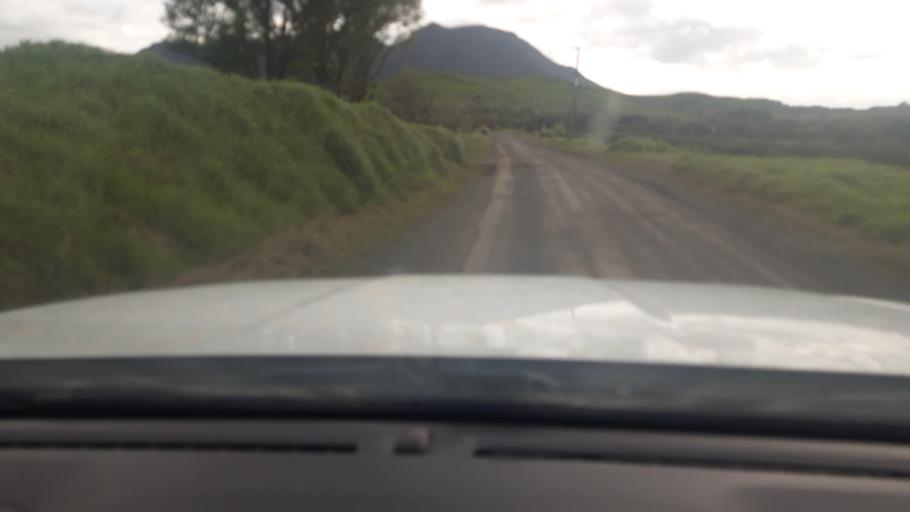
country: NZ
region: Northland
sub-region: Far North District
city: Ahipara
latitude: -35.2578
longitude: 173.2030
